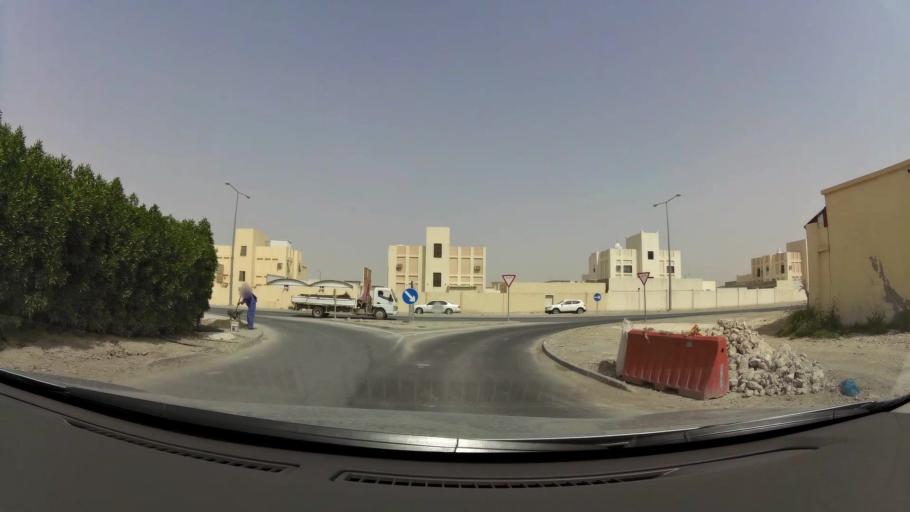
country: QA
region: Baladiyat ar Rayyan
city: Ar Rayyan
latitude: 25.2392
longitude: 51.3807
